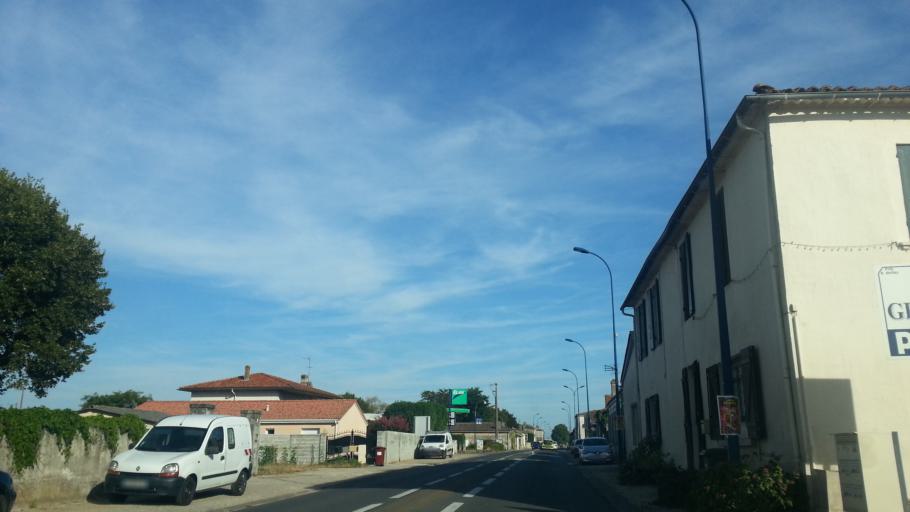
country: FR
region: Aquitaine
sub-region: Departement de la Gironde
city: Portets
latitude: 44.6884
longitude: -0.4178
